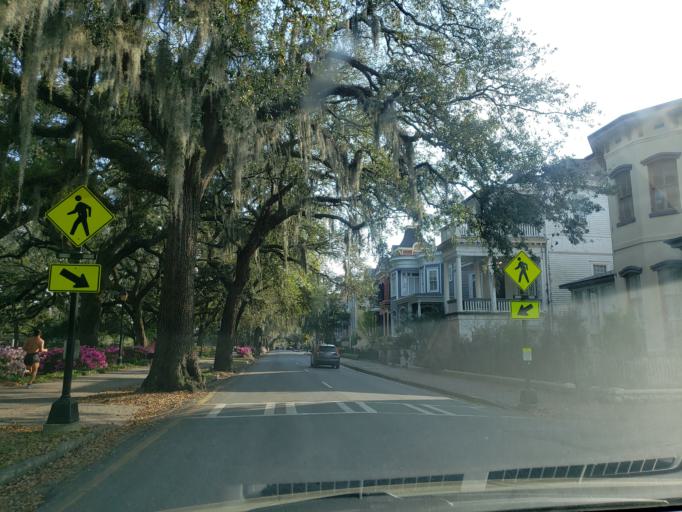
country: US
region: Georgia
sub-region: Hall County
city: Oakwood
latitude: 34.2599
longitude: -83.9412
